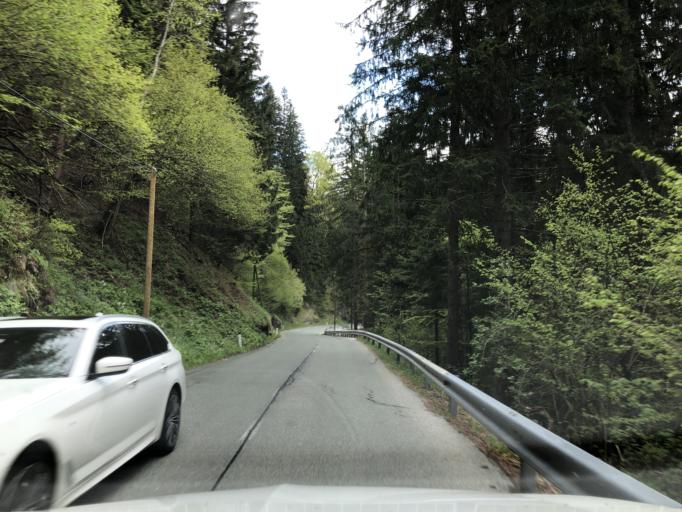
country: SI
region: Kranjska Gora
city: Kranjska Gora
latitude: 46.5020
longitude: 13.7552
